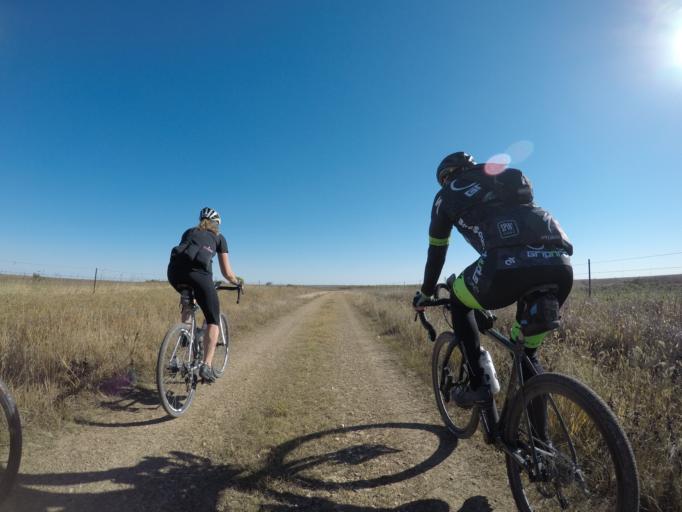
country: US
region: Kansas
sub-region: Wabaunsee County
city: Alma
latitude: 38.8825
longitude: -96.3893
